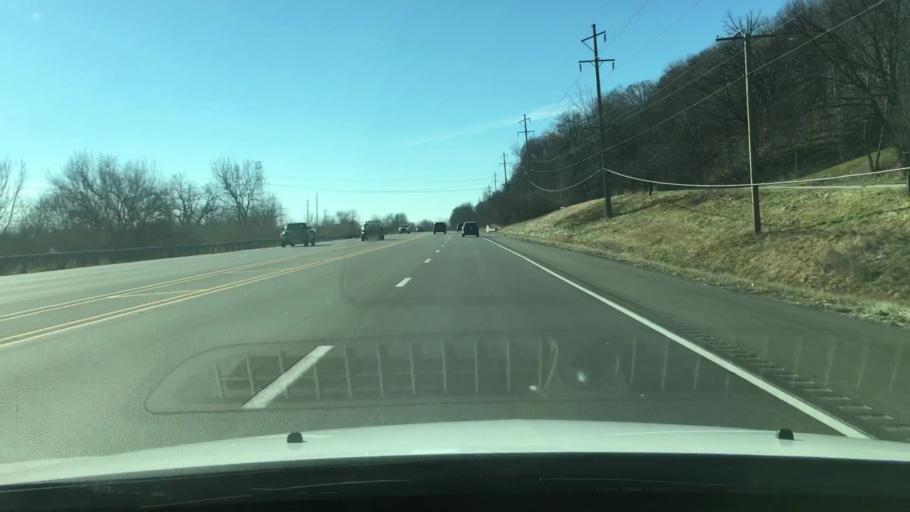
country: US
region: Illinois
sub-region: Tazewell County
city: Pekin
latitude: 40.6003
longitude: -89.6683
